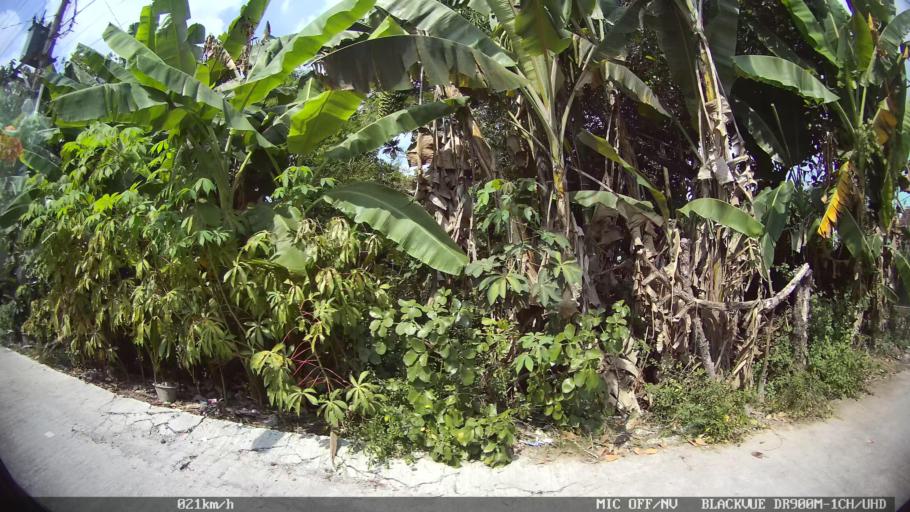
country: ID
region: Daerah Istimewa Yogyakarta
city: Kasihan
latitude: -7.8147
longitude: 110.3363
